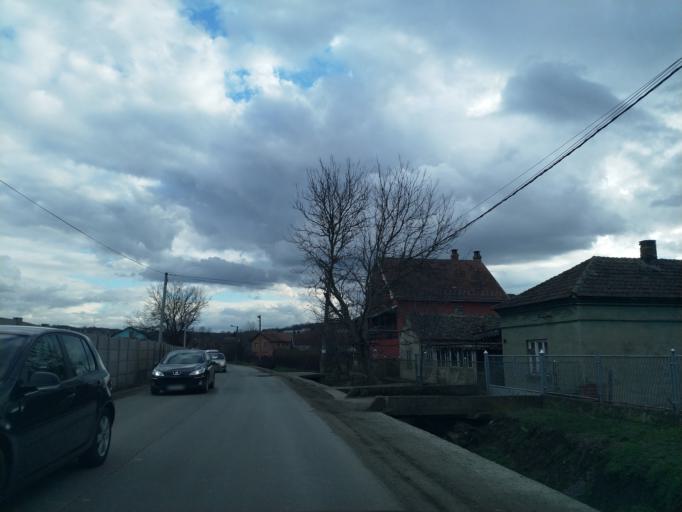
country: RS
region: Central Serbia
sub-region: Belgrade
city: Grocka
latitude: 44.5780
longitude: 20.7407
